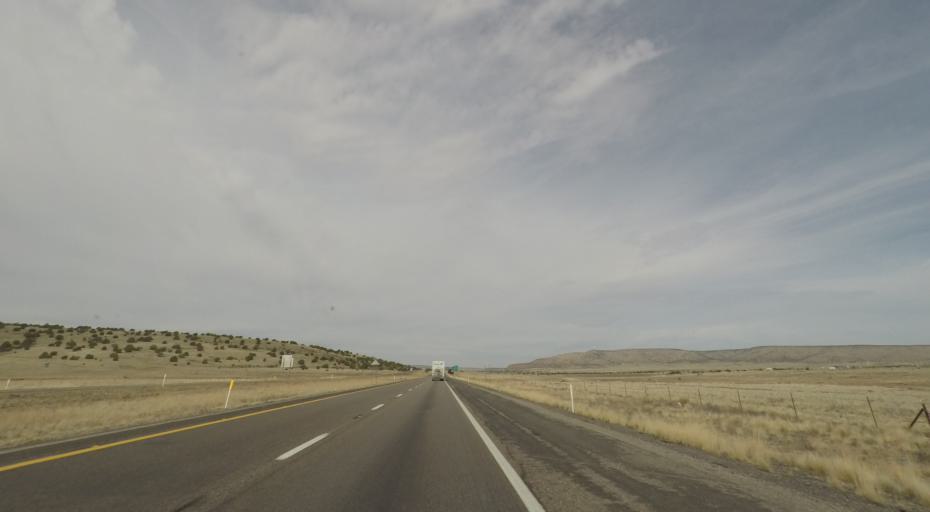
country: US
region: Arizona
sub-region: Mohave County
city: Peach Springs
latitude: 35.3169
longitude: -112.8735
